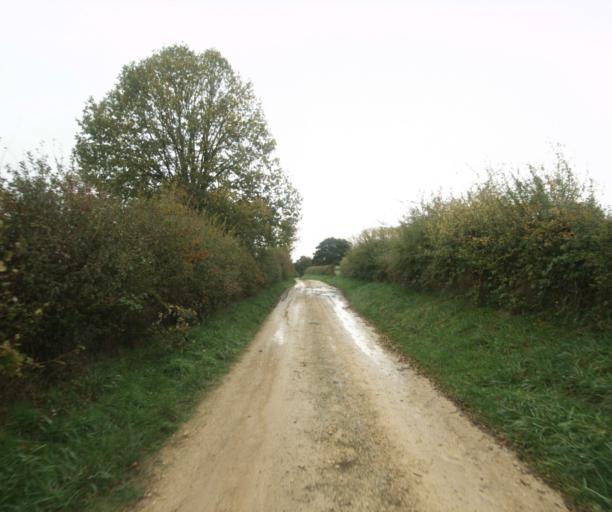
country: FR
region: Rhone-Alpes
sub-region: Departement de l'Ain
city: Pont-de-Vaux
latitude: 46.4824
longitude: 4.8747
